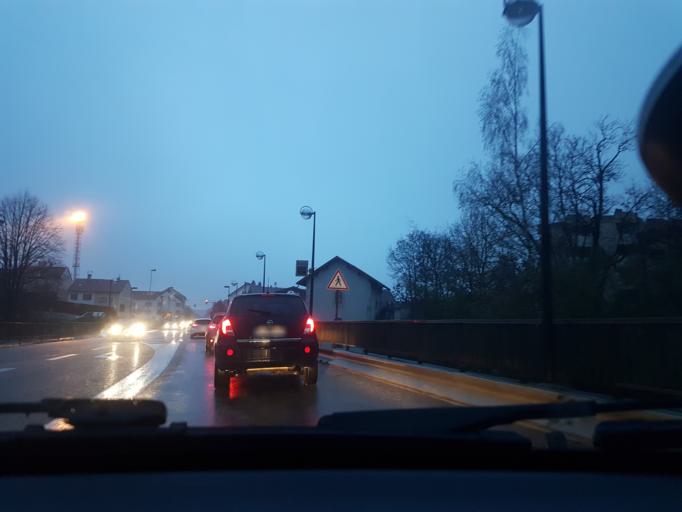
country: FR
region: Franche-Comte
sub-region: Departement du Doubs
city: Pontarlier
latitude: 46.9000
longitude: 6.3586
